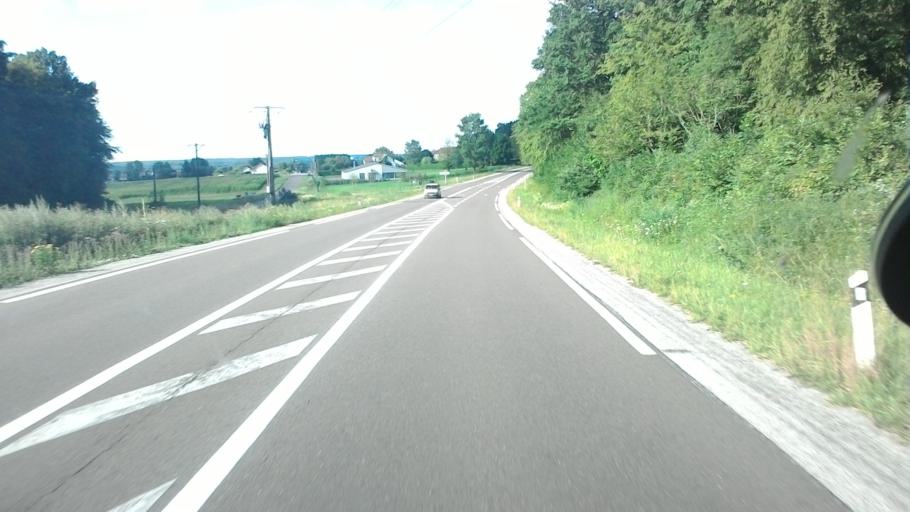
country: FR
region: Franche-Comte
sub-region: Departement de la Haute-Saone
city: Luxeuil-les-Bains
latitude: 47.7663
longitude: 6.3415
